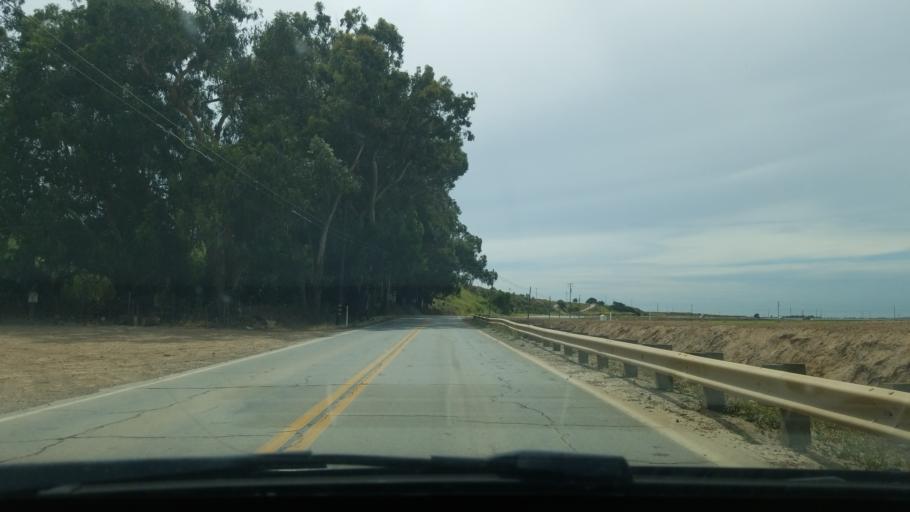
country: US
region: California
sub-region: Santa Barbara County
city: Orcutt
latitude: 34.9086
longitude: -120.3415
